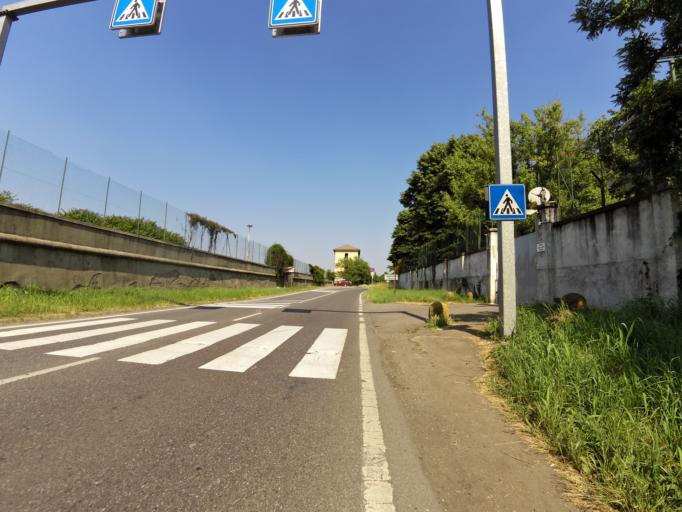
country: IT
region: Lombardy
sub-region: Citta metropolitana di Milano
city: Novegro-Tregarezzo-San Felice
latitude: 45.4723
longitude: 9.2692
